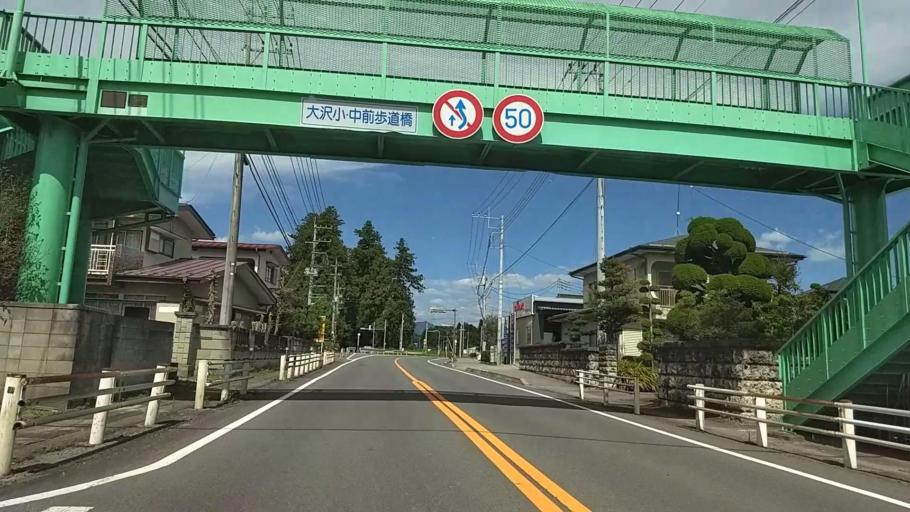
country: JP
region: Tochigi
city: Imaichi
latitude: 36.6962
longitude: 139.7561
